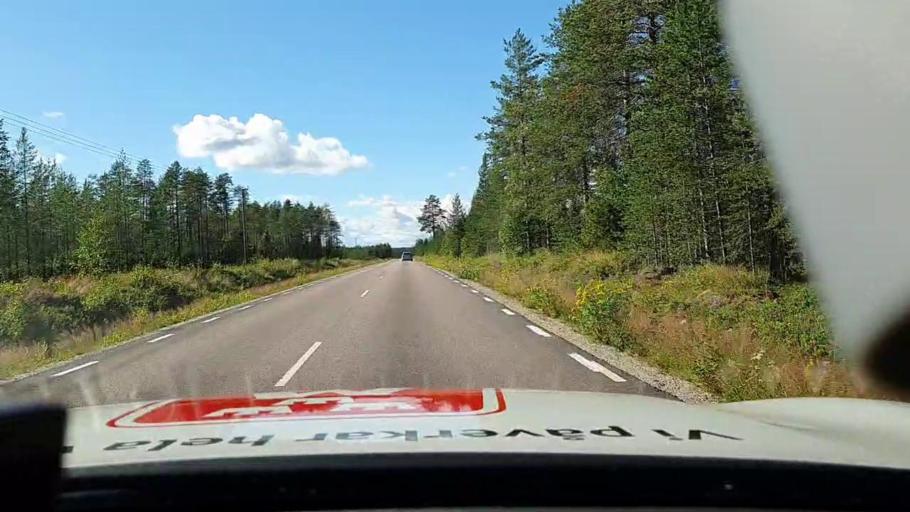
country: SE
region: Norrbotten
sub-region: Overkalix Kommun
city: OEverkalix
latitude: 66.2553
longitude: 22.8646
